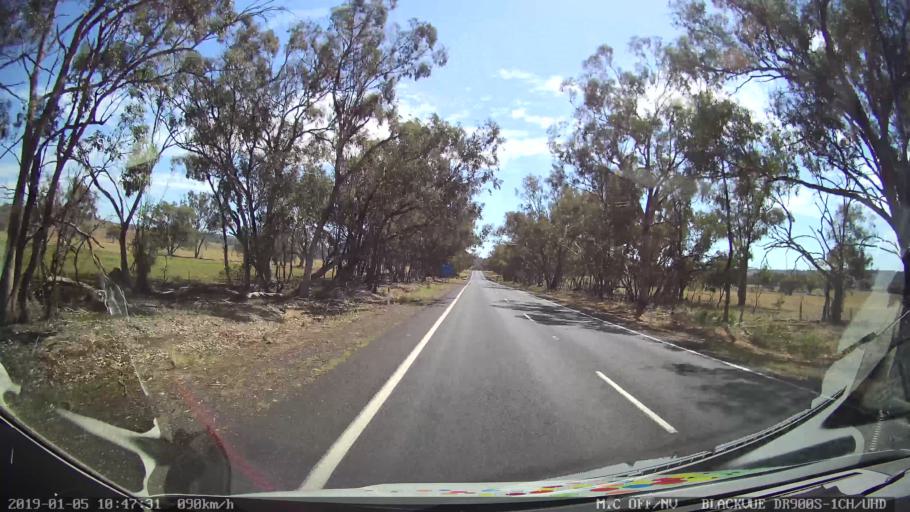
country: AU
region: New South Wales
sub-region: Warrumbungle Shire
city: Coonabarabran
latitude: -31.4444
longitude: 149.0339
